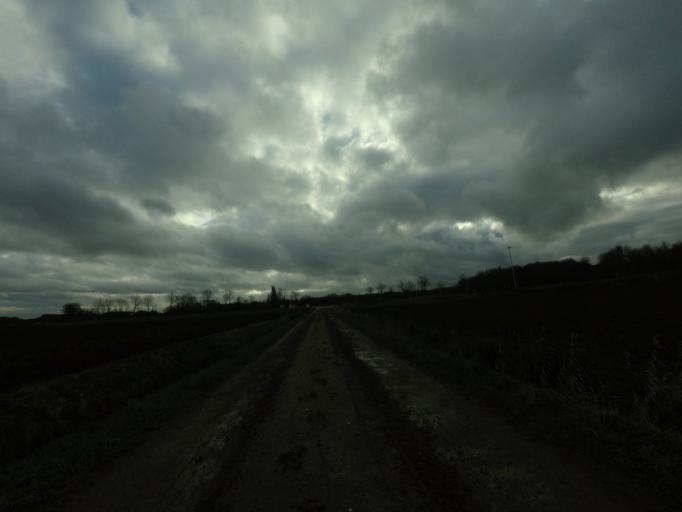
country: NL
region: North Brabant
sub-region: Gemeente Woensdrecht
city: Woensdrecht
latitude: 51.3695
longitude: 4.3204
